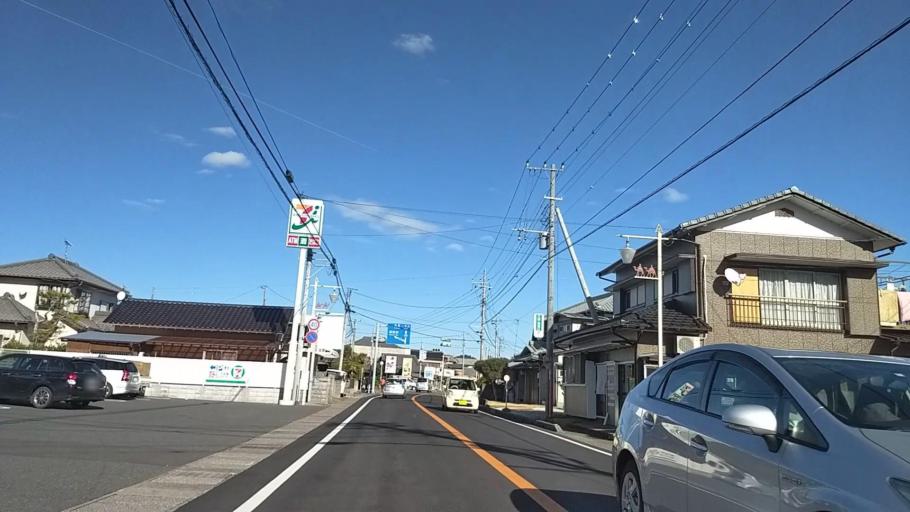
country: JP
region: Chiba
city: Katsuura
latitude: 35.1838
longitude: 140.3499
